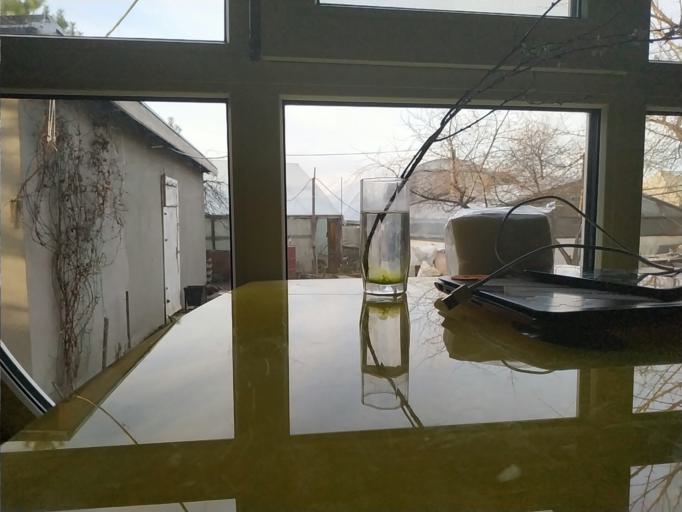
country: RU
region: Republic of Karelia
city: Suoyarvi
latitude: 62.1262
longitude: 32.1519
